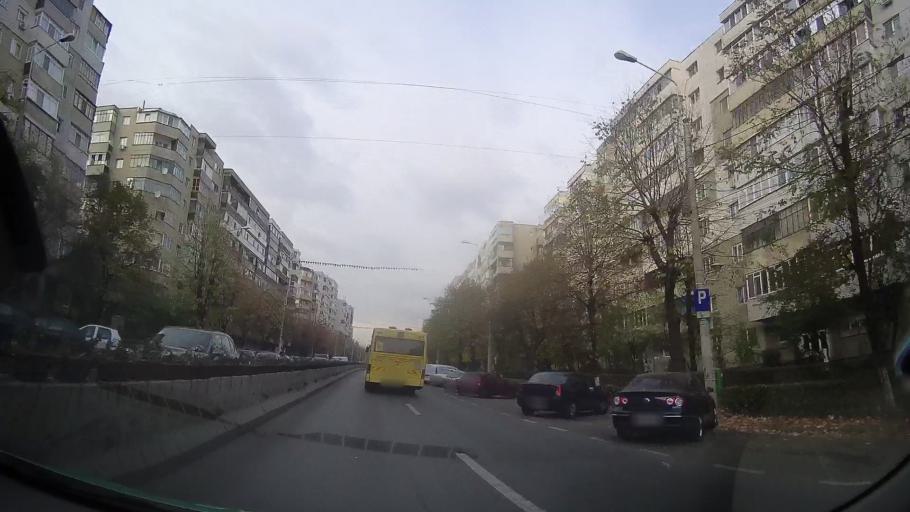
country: RO
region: Prahova
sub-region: Comuna Barcanesti
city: Tatarani
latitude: 44.9192
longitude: 26.0346
